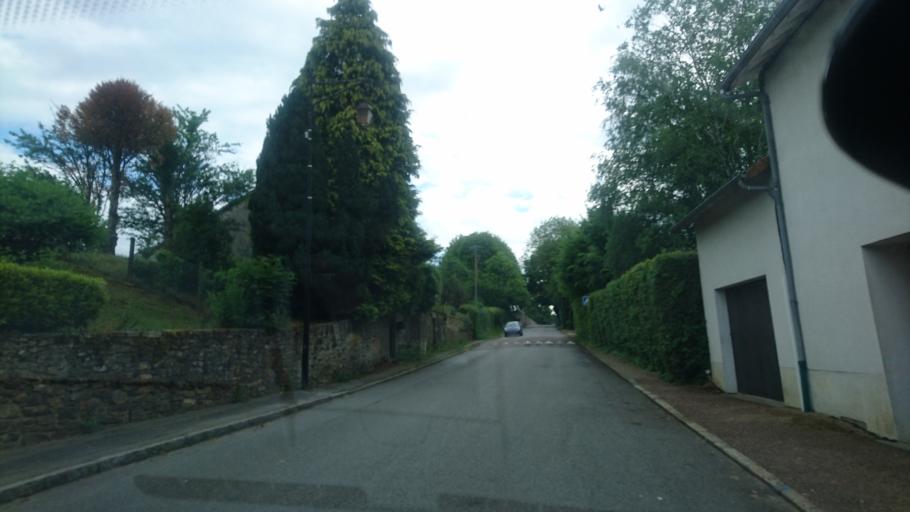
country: FR
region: Limousin
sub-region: Departement de la Haute-Vienne
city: Saint-Germain-les-Belles
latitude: 45.6171
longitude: 1.4972
